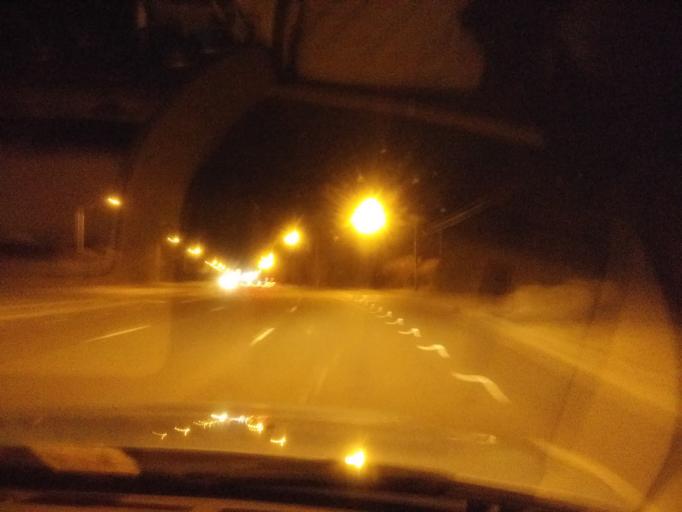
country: US
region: Virginia
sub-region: City of Chesapeake
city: Chesapeake
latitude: 36.7765
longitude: -76.1987
